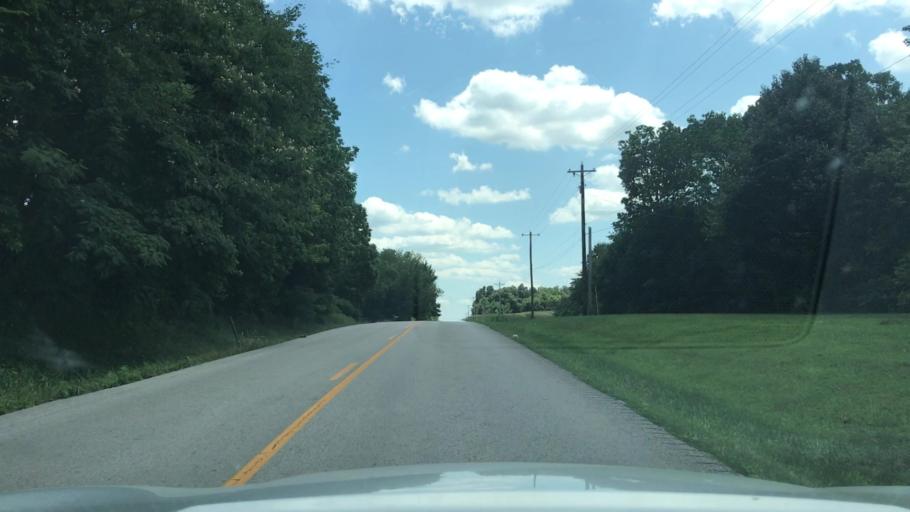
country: US
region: Kentucky
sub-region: Christian County
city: Hopkinsville
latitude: 36.9947
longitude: -87.3639
